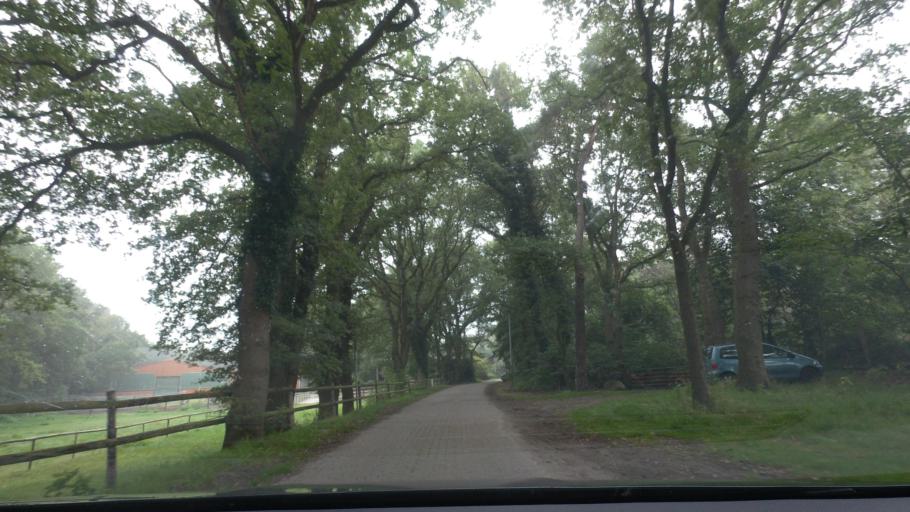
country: DE
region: Lower Saxony
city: Hude
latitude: 53.1209
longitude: 8.4441
